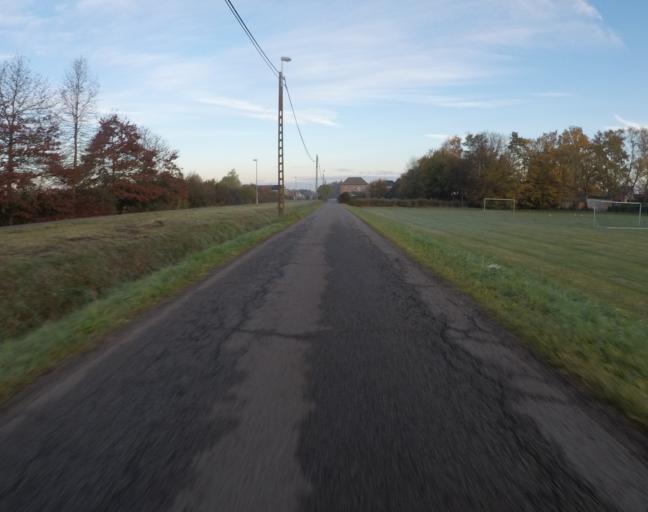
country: BE
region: Flanders
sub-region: Provincie Vlaams-Brabant
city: Aarschot
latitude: 51.0298
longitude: 4.8267
